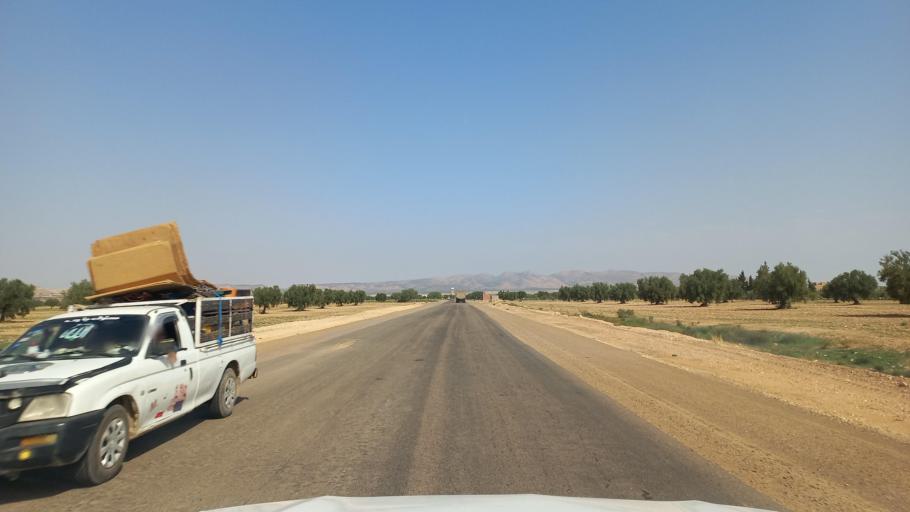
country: TN
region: Al Qasrayn
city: Sbiba
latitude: 35.3451
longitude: 9.0547
